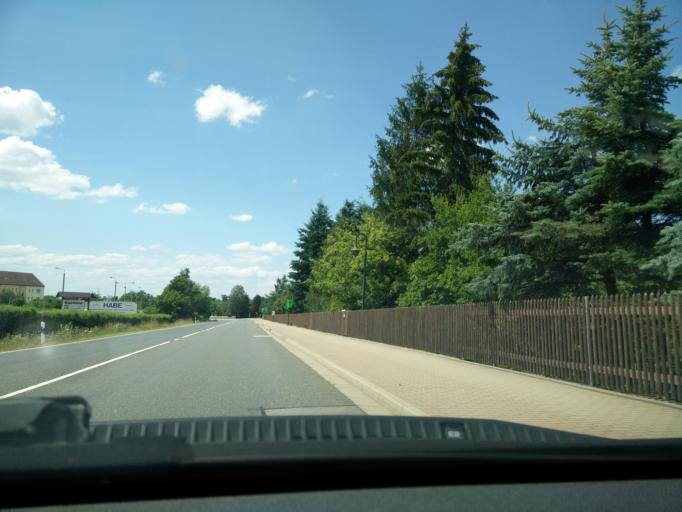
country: DE
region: Saxony
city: Muhlau
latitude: 50.8989
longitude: 12.7710
